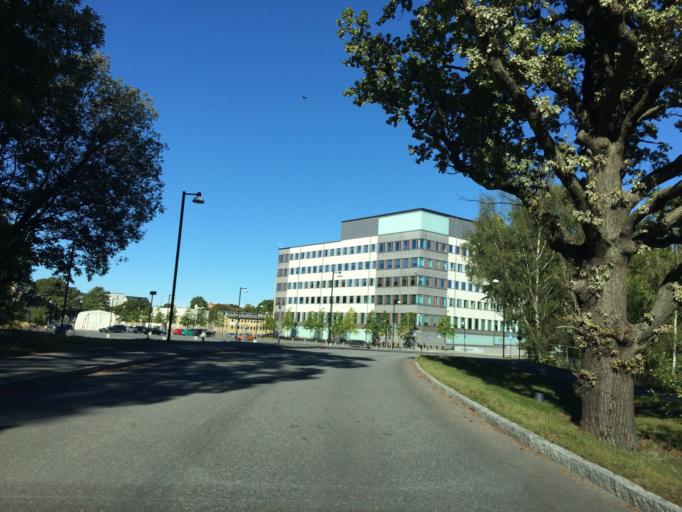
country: SE
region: Stockholm
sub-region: Solna Kommun
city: Solna
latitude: 59.3509
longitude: 18.0117
